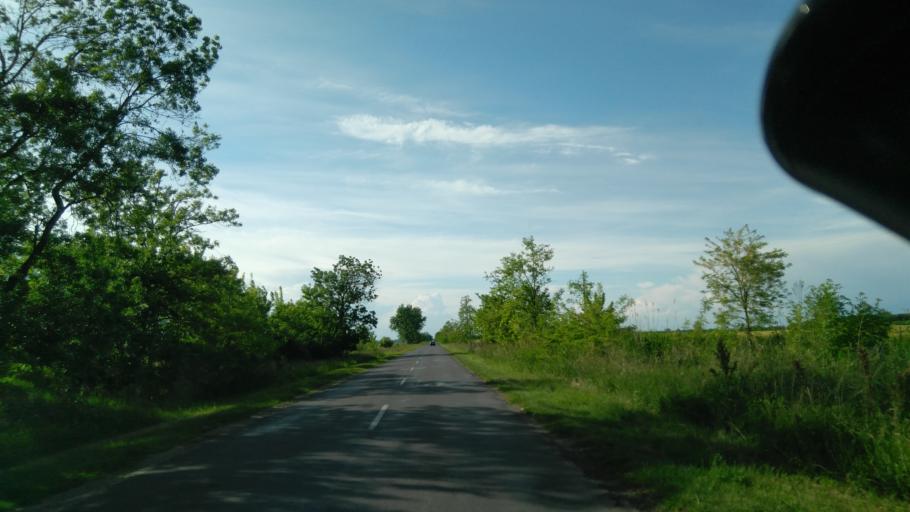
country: HU
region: Bekes
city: Lokoshaza
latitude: 46.4461
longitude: 21.2208
